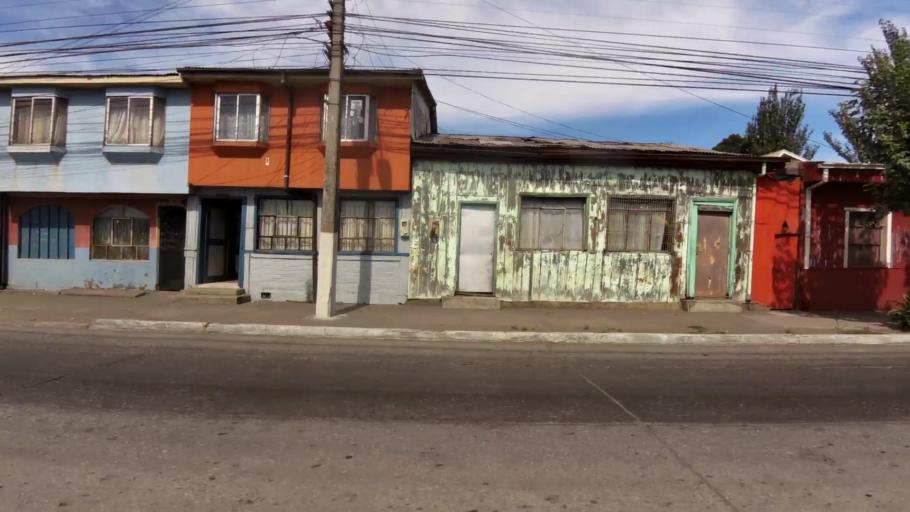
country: CL
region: Biobio
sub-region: Provincia de Concepcion
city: Talcahuano
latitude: -36.7262
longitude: -73.1168
